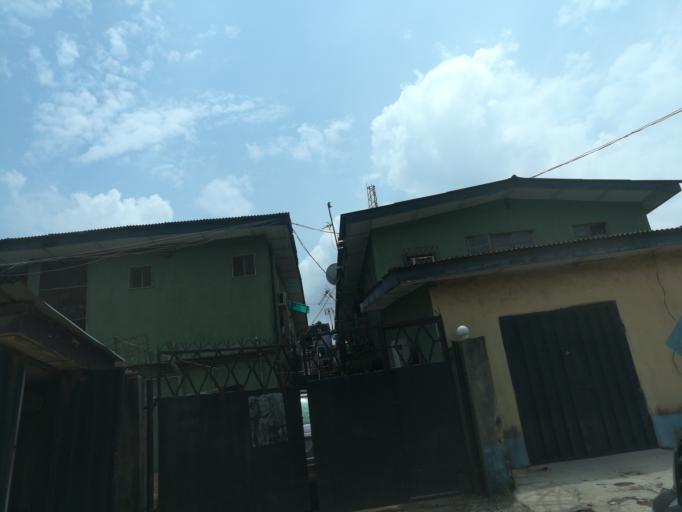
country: NG
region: Lagos
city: Oshodi
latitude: 6.5512
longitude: 3.3267
